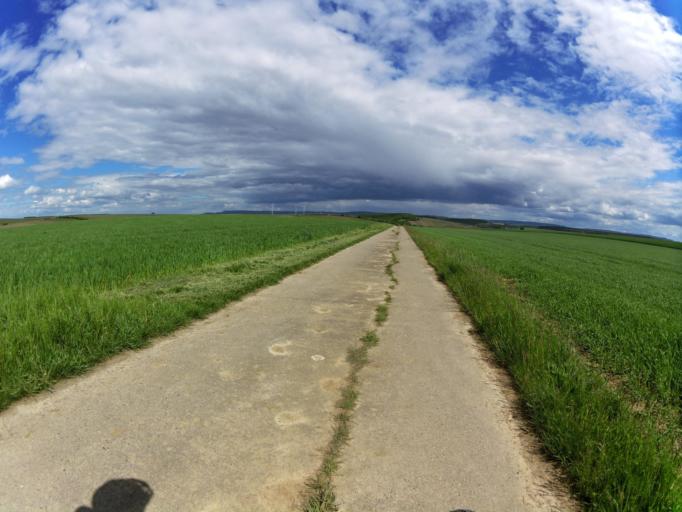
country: DE
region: Bavaria
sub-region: Regierungsbezirk Unterfranken
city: Volkach
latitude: 49.8827
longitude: 10.2290
